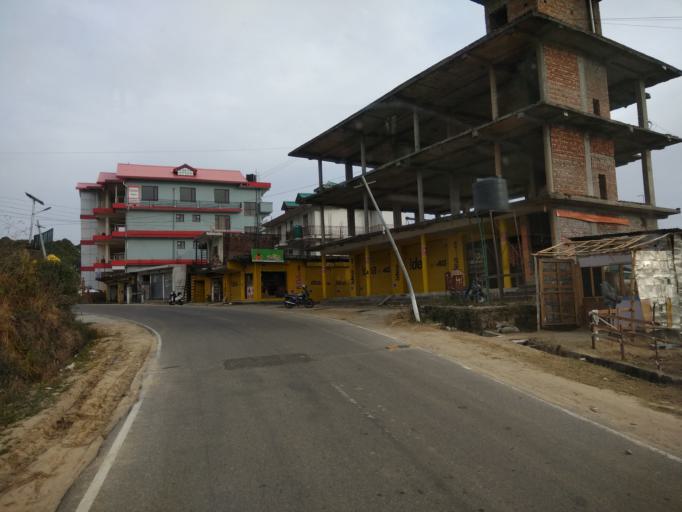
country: IN
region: Himachal Pradesh
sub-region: Kangra
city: Palampur
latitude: 32.1113
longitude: 76.5018
